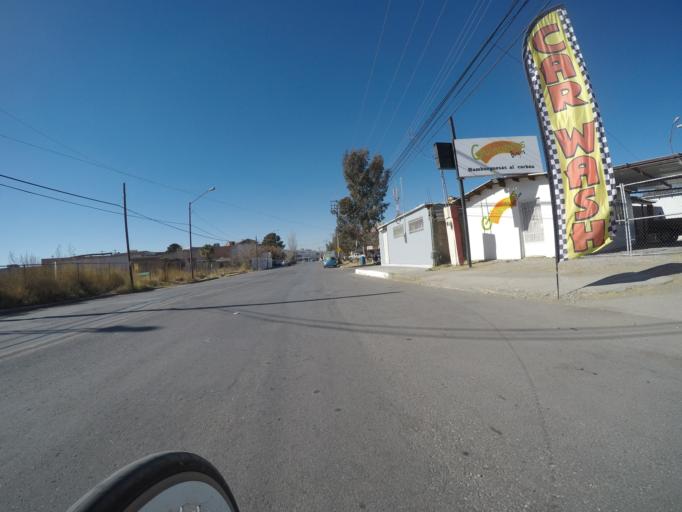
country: MX
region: Chihuahua
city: Ciudad Juarez
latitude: 31.7140
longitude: -106.4178
